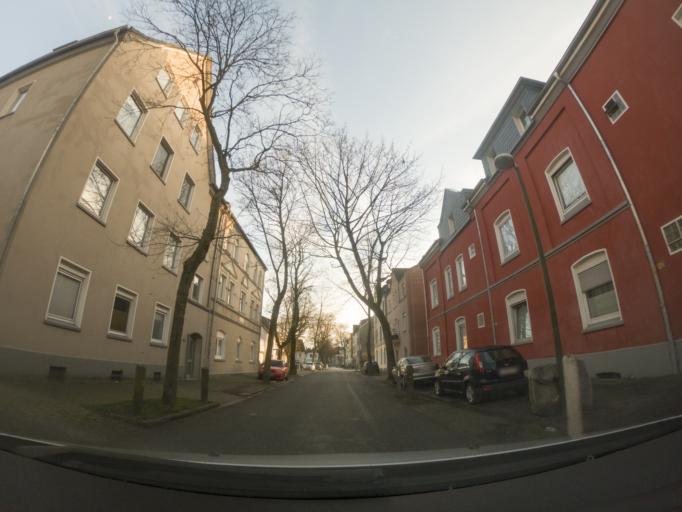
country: DE
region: North Rhine-Westphalia
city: Waltrop
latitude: 51.5953
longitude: 7.4434
